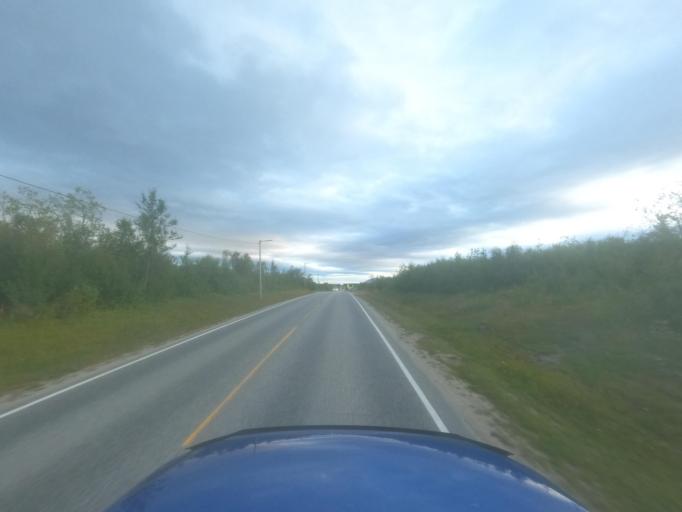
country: NO
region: Finnmark Fylke
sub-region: Porsanger
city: Lakselv
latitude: 70.0479
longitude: 24.9784
